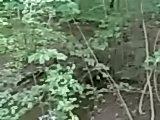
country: RU
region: Kaliningrad
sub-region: Gorod Kaliningrad
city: Kaliningrad
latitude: 54.6659
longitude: 20.5222
